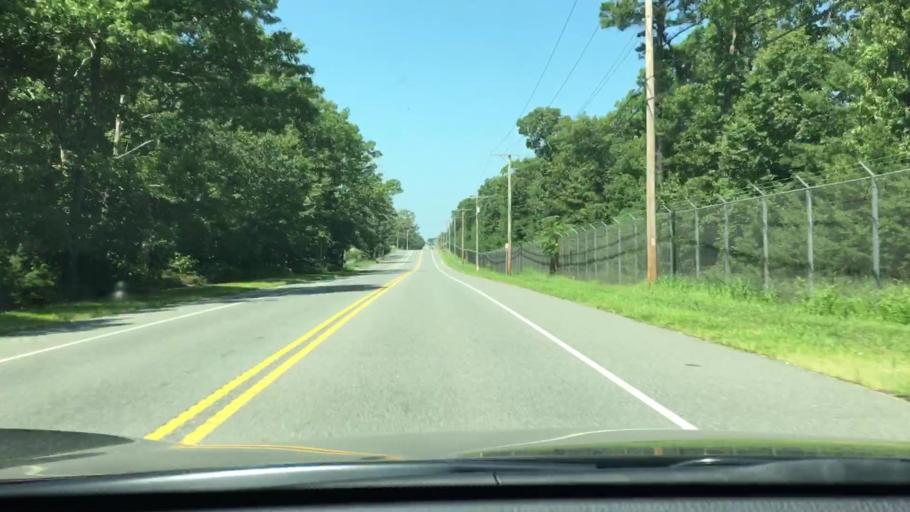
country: US
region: New Jersey
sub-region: Cumberland County
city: Laurel Lake
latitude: 39.3579
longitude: -75.0696
